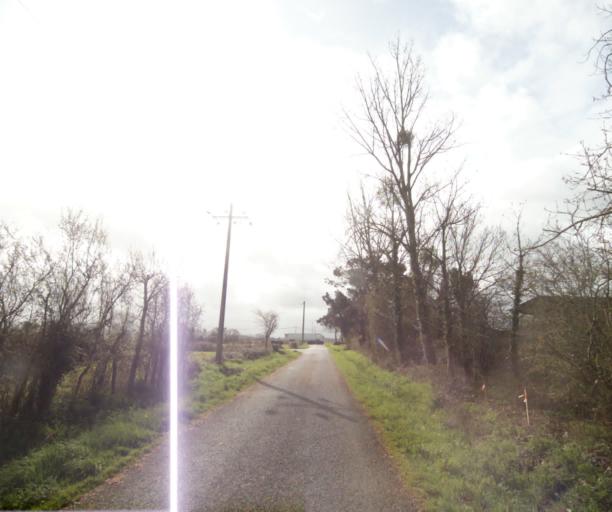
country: FR
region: Pays de la Loire
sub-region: Departement de la Loire-Atlantique
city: Bouvron
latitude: 47.4111
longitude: -1.8551
